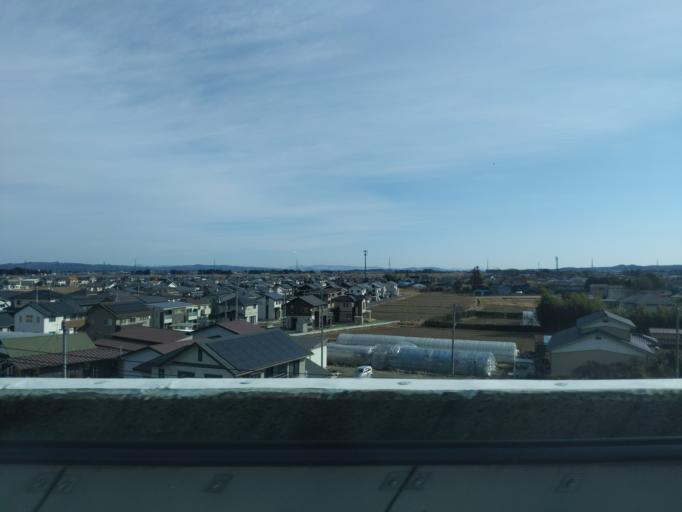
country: JP
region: Miyagi
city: Furukawa
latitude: 38.5599
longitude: 140.9649
